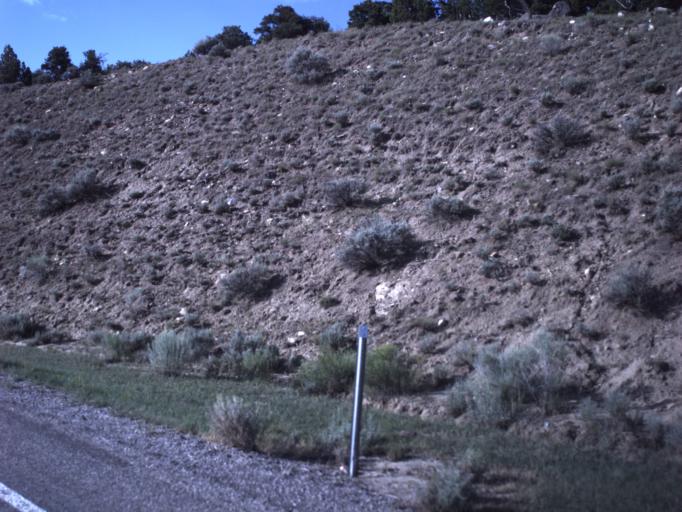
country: US
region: Utah
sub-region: Wayne County
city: Loa
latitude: 38.7247
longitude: -111.4002
